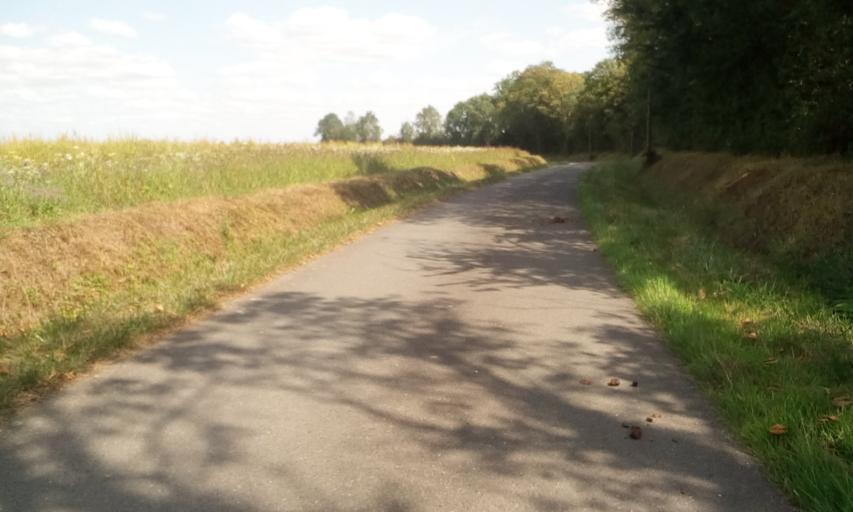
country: FR
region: Lower Normandy
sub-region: Departement du Calvados
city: Argences
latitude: 49.1320
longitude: -0.1248
